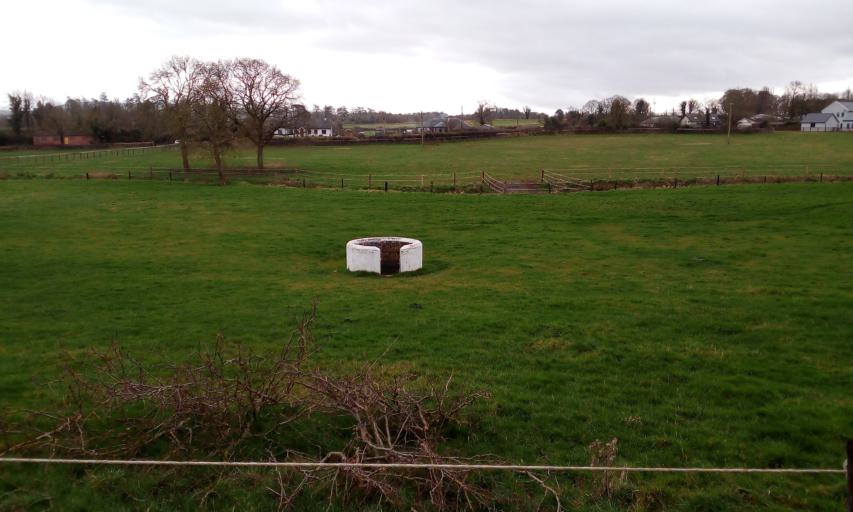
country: IE
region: Leinster
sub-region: Kilkenny
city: Thomastown
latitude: 52.6277
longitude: -7.0748
